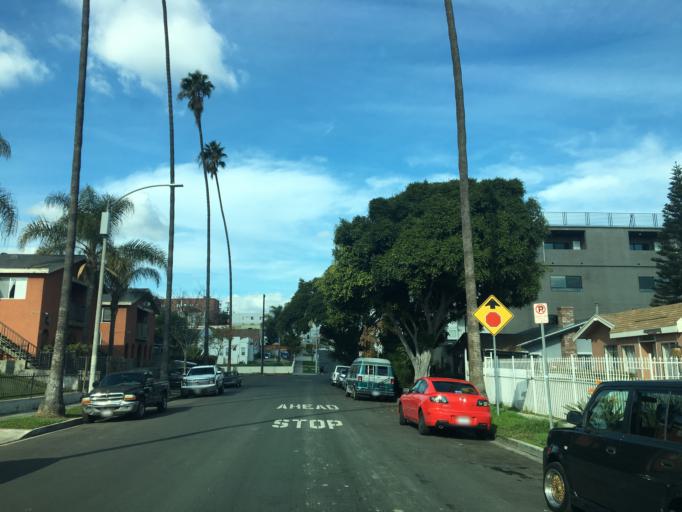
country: US
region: California
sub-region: Los Angeles County
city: Silver Lake
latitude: 34.0745
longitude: -118.2984
